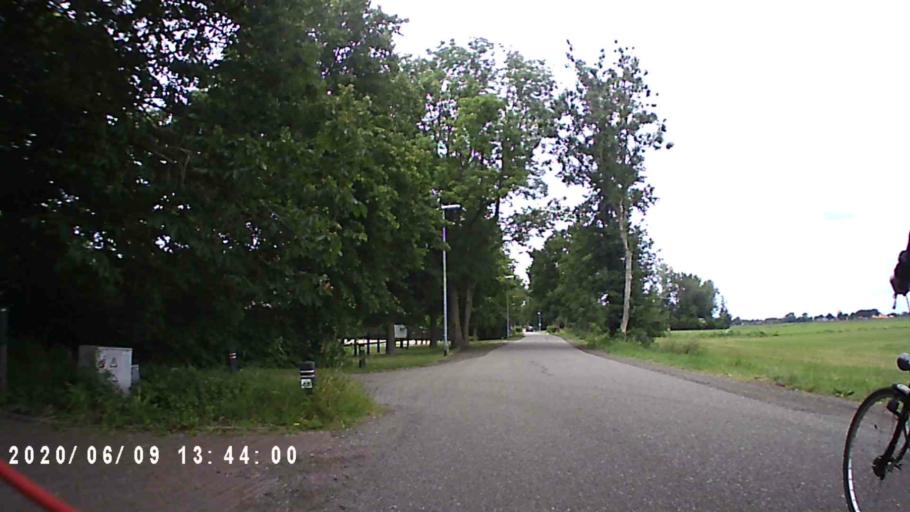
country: NL
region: Groningen
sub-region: Gemeente Groningen
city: Oosterpark
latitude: 53.2184
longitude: 6.6396
